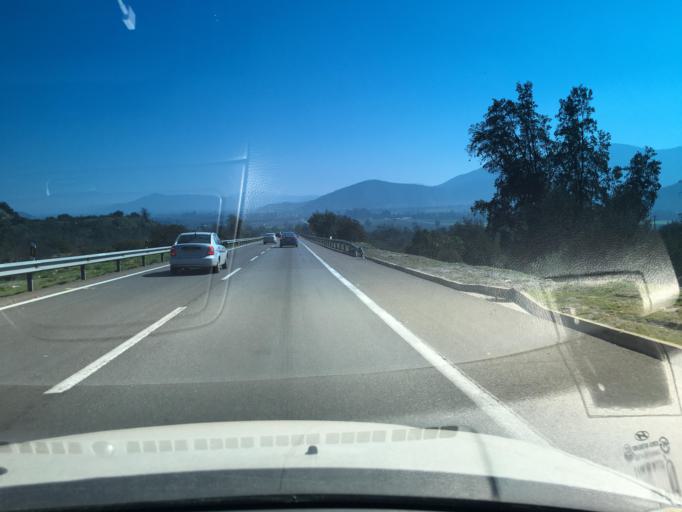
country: CL
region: Santiago Metropolitan
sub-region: Provincia de Melipilla
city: Melipilla
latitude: -33.3836
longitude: -71.2758
